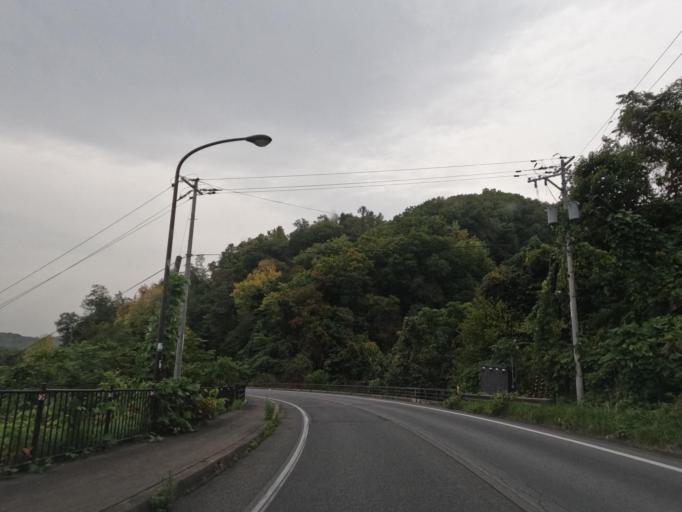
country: JP
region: Hokkaido
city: Date
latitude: 42.5273
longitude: 140.8614
